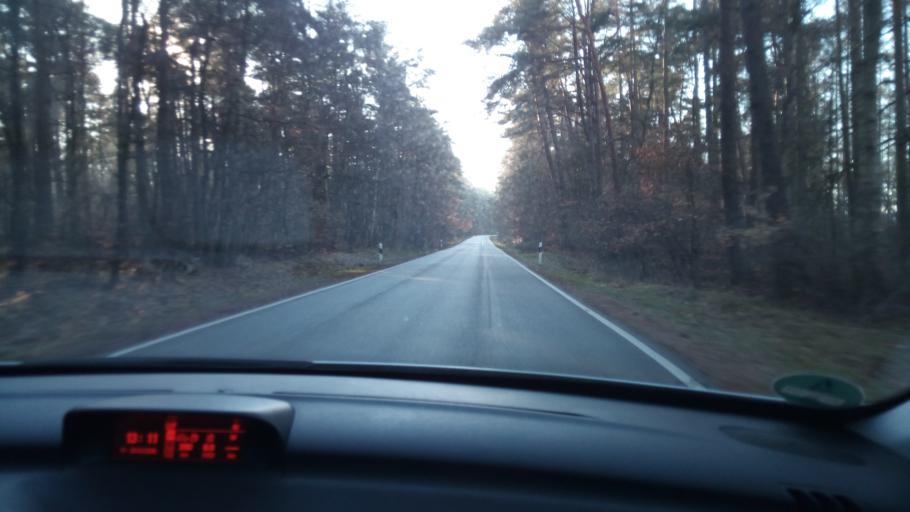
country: DE
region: Schleswig-Holstein
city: Gottin
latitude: 53.5146
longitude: 10.6971
